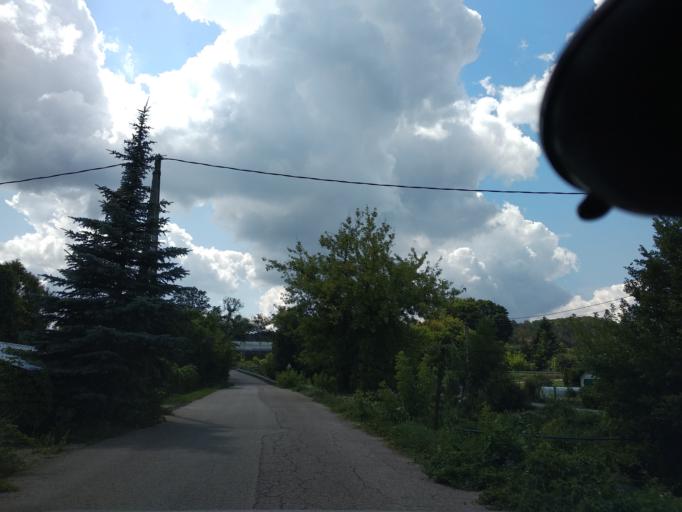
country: LT
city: Grigiskes
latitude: 54.6799
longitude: 25.0779
